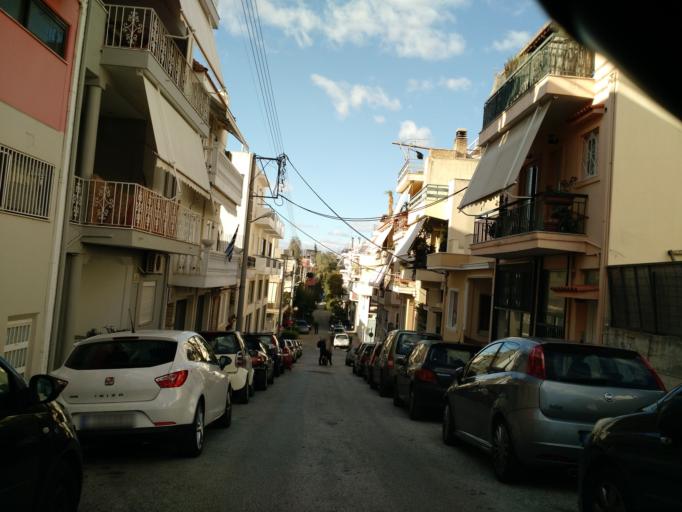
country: GR
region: Attica
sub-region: Nomarchia Athinas
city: Agios Dimitrios
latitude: 37.9376
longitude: 23.7392
